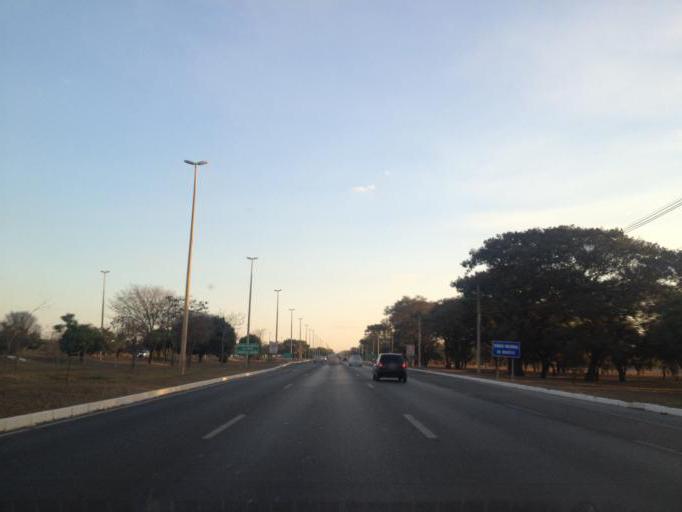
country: BR
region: Federal District
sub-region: Brasilia
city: Brasilia
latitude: -15.7399
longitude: -47.9170
